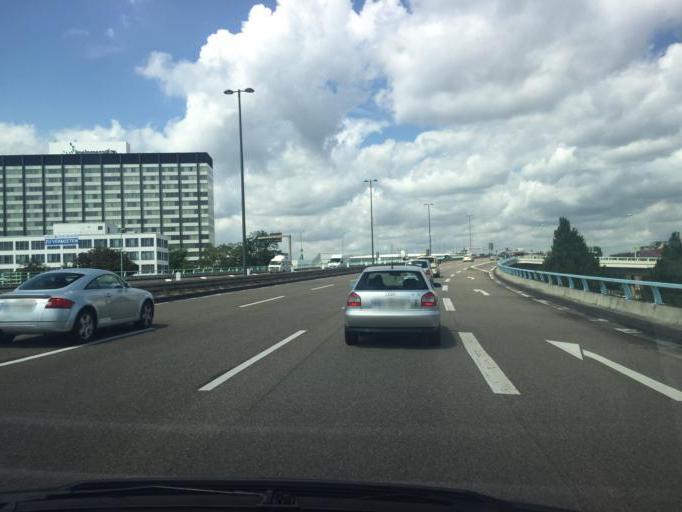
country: DE
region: North Rhine-Westphalia
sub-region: Regierungsbezirk Koln
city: Humboldtkolonie
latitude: 50.9464
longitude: 6.9871
